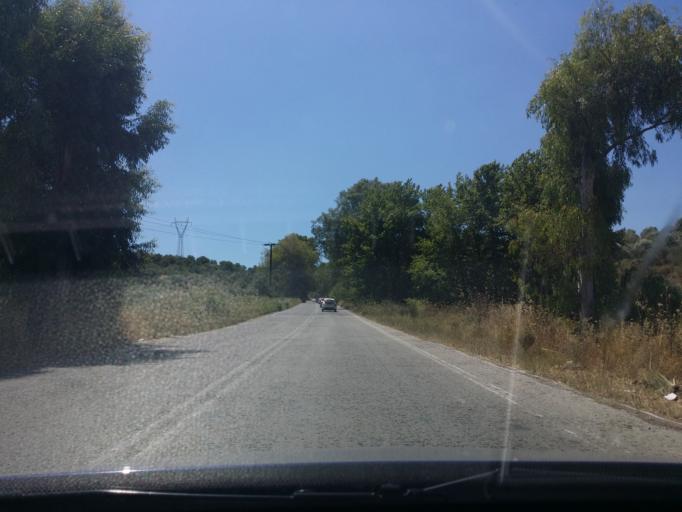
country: GR
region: Peloponnese
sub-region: Nomos Lakonias
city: Krokeai
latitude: 36.9560
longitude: 22.5077
